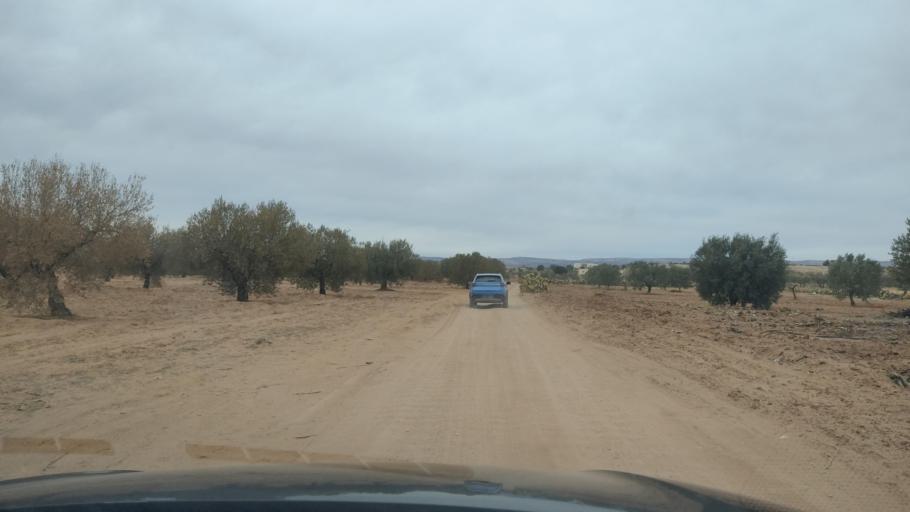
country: TN
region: Al Qasrayn
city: Kasserine
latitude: 35.2269
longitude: 8.9183
